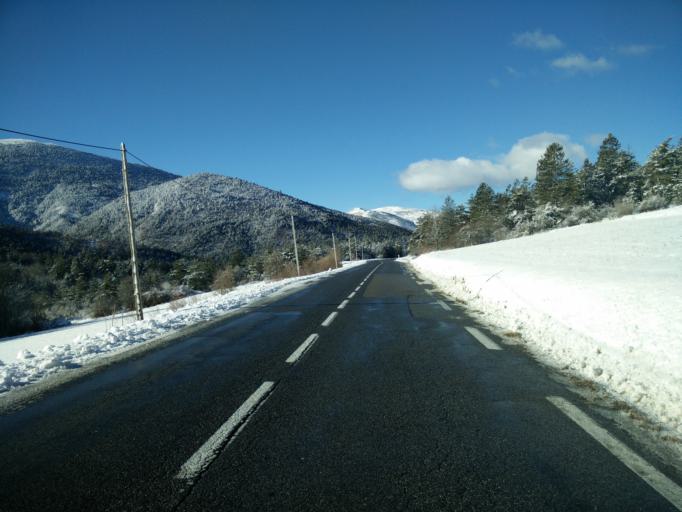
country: FR
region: Provence-Alpes-Cote d'Azur
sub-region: Departement des Alpes-de-Haute-Provence
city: Annot
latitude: 43.9124
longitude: 6.6042
